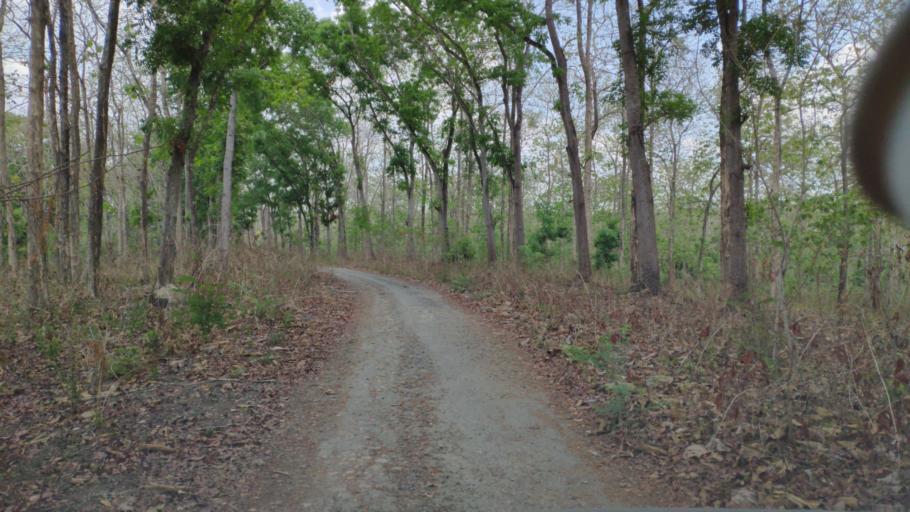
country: ID
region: Central Java
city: Singonegoro
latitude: -6.9922
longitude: 111.5336
